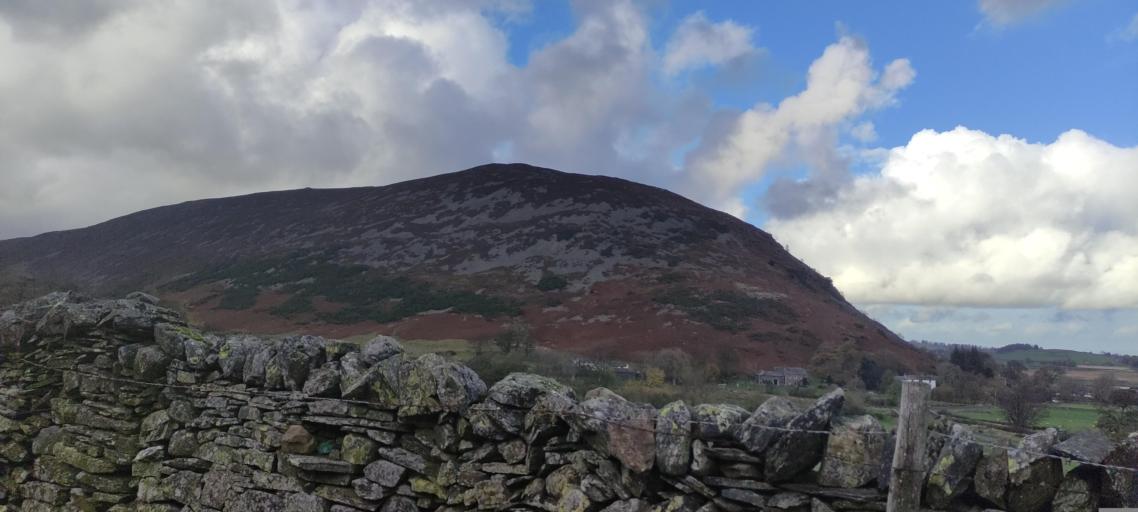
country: GB
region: England
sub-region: Cumbria
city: Keswick
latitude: 54.6762
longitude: -2.9989
